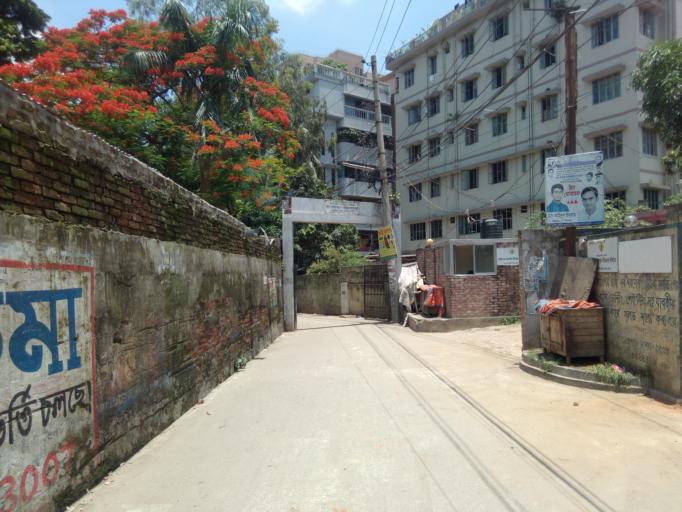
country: BD
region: Dhaka
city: Paltan
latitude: 23.7555
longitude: 90.4007
